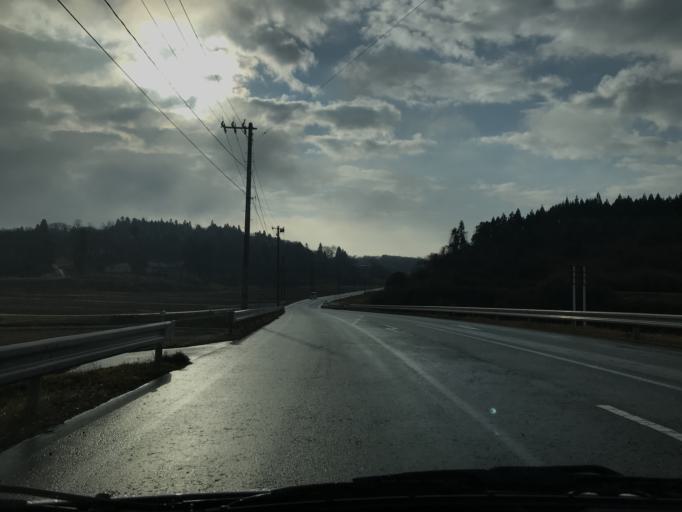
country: JP
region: Iwate
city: Ichinoseki
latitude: 38.8998
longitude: 141.1583
